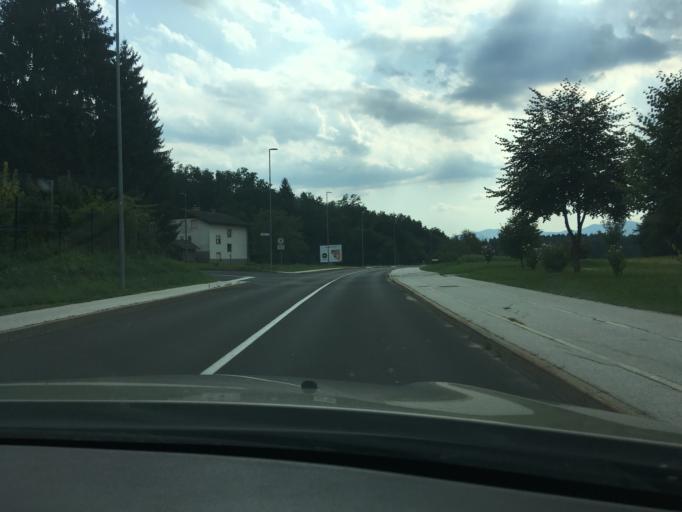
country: SI
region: Novo Mesto
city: Novo Mesto
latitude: 45.7969
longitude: 15.1479
